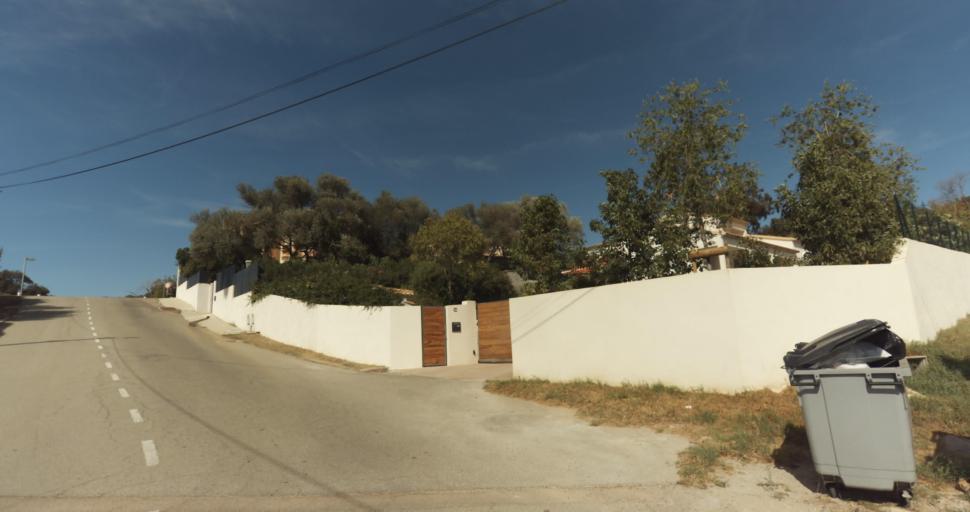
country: FR
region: Corsica
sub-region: Departement de la Corse-du-Sud
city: Ajaccio
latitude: 41.9406
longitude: 8.7648
